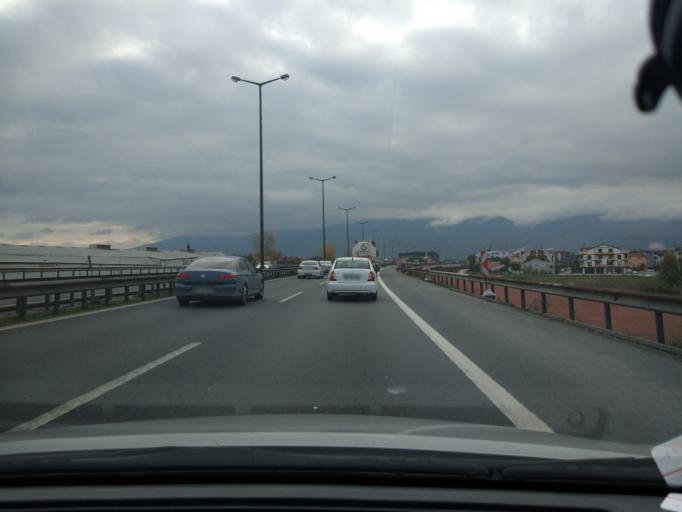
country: TR
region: Kocaeli
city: Kosekoy
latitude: 40.7592
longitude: 30.0356
